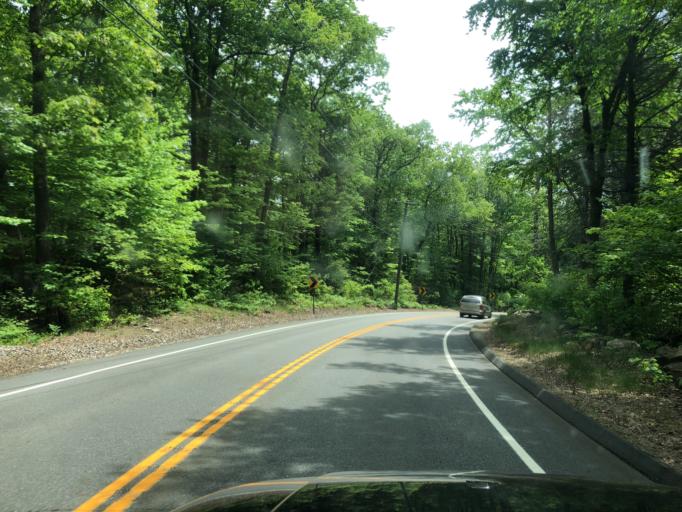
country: US
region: Massachusetts
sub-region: Hampden County
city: Holland
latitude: 41.9949
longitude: -72.1495
